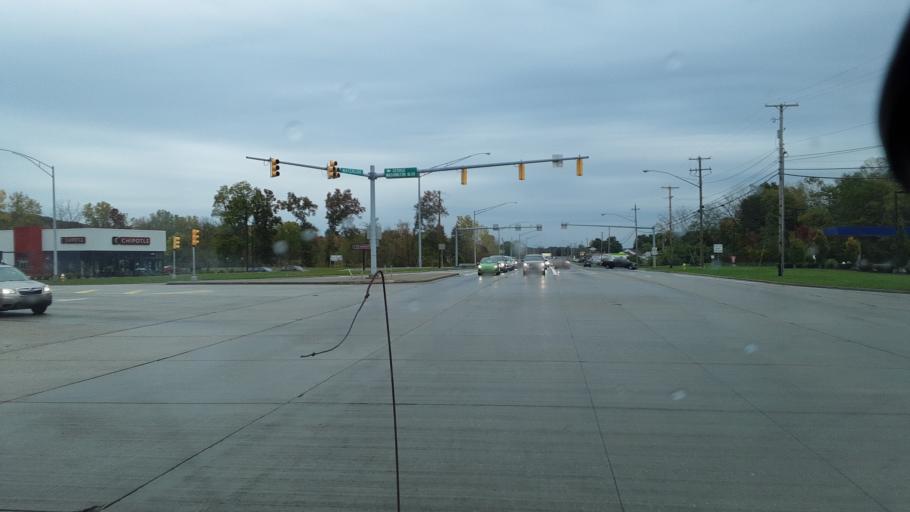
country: US
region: Ohio
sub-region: Summit County
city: Sawyerwood
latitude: 41.0273
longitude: -81.4625
